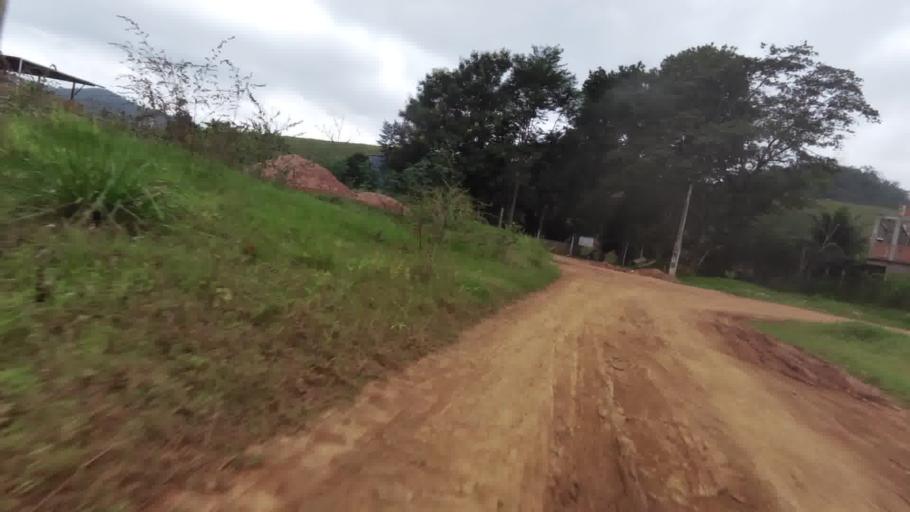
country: BR
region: Espirito Santo
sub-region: Alfredo Chaves
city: Alfredo Chaves
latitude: -20.6413
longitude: -40.7432
